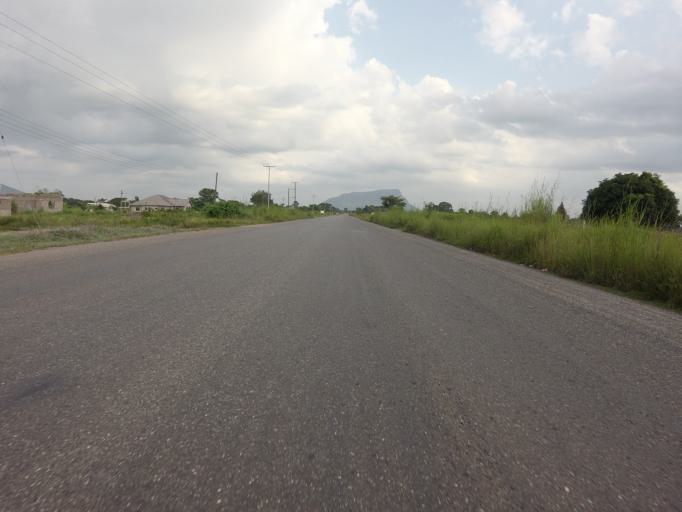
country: GH
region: Volta
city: Ho
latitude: 6.5707
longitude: 0.4853
